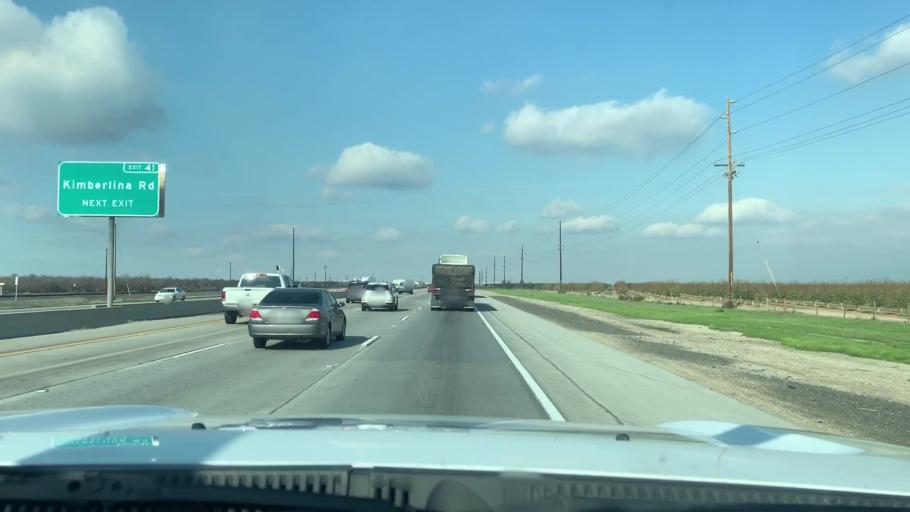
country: US
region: California
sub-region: Kern County
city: Shafter
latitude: 35.5437
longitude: -119.1945
